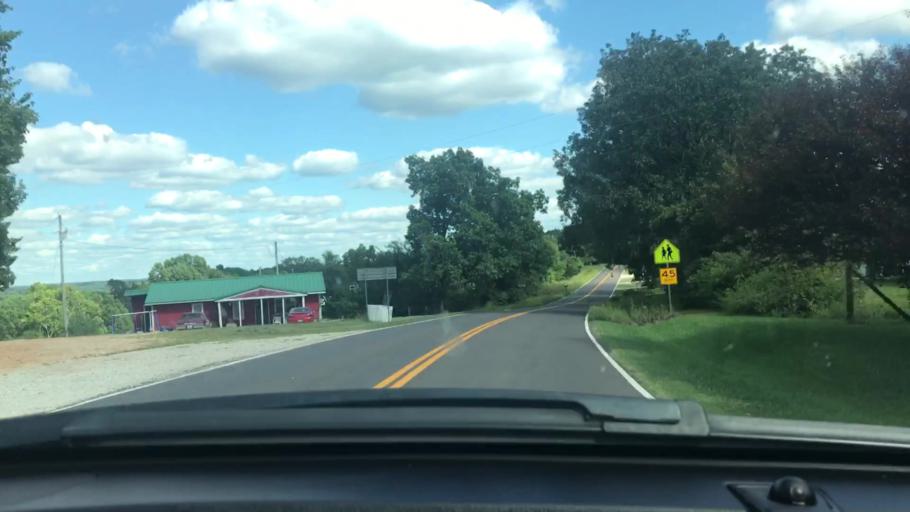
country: US
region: Missouri
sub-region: Wright County
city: Hartville
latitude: 37.3796
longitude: -92.3617
